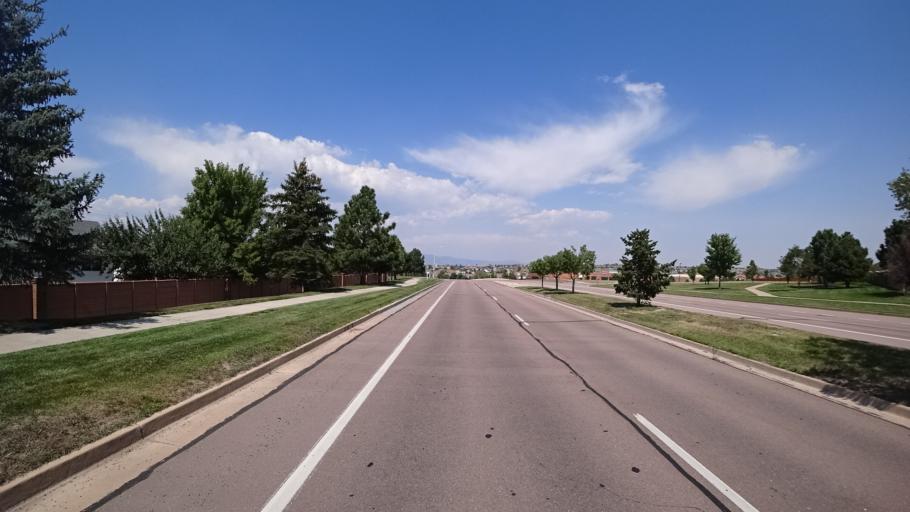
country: US
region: Colorado
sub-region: El Paso County
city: Cimarron Hills
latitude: 38.9303
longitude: -104.7376
